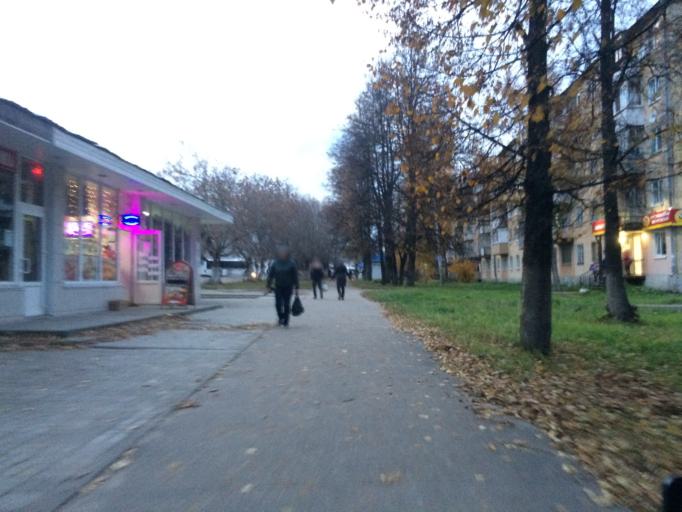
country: RU
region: Mariy-El
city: Yoshkar-Ola
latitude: 56.6204
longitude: 47.8851
